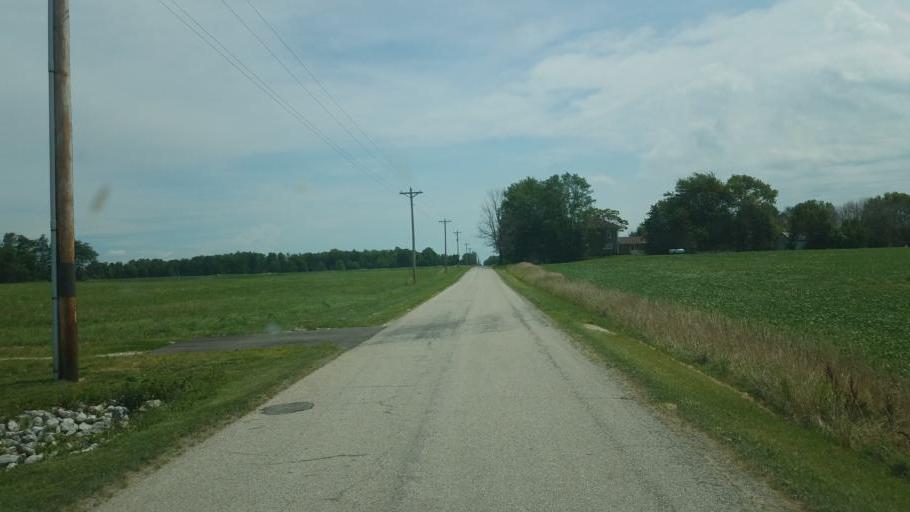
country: US
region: Ohio
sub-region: Crawford County
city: Bucyrus
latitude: 40.8775
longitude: -83.0255
